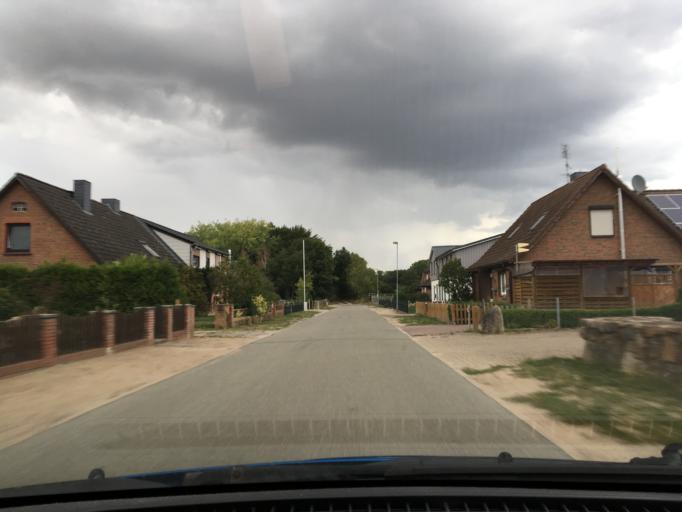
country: DE
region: Schleswig-Holstein
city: Lanze
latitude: 53.3914
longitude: 10.6076
